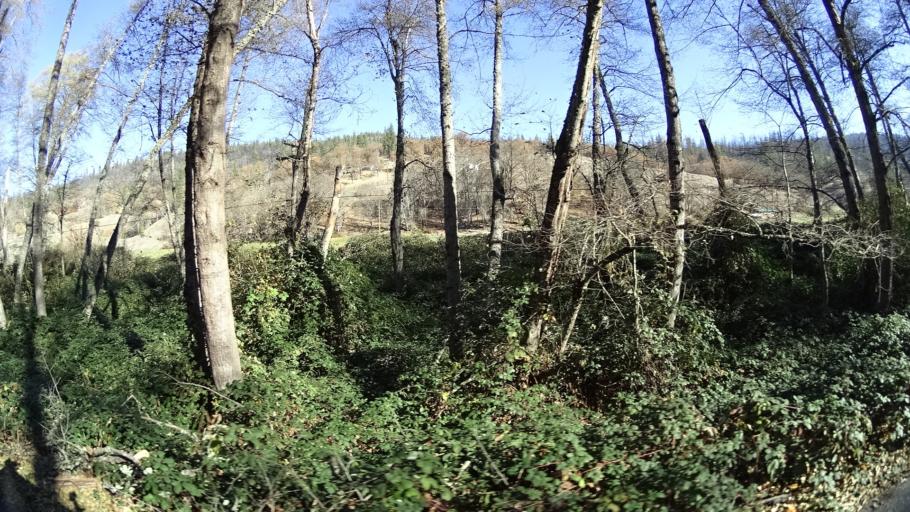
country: US
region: California
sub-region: Siskiyou County
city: Happy Camp
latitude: 41.8401
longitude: -123.0181
